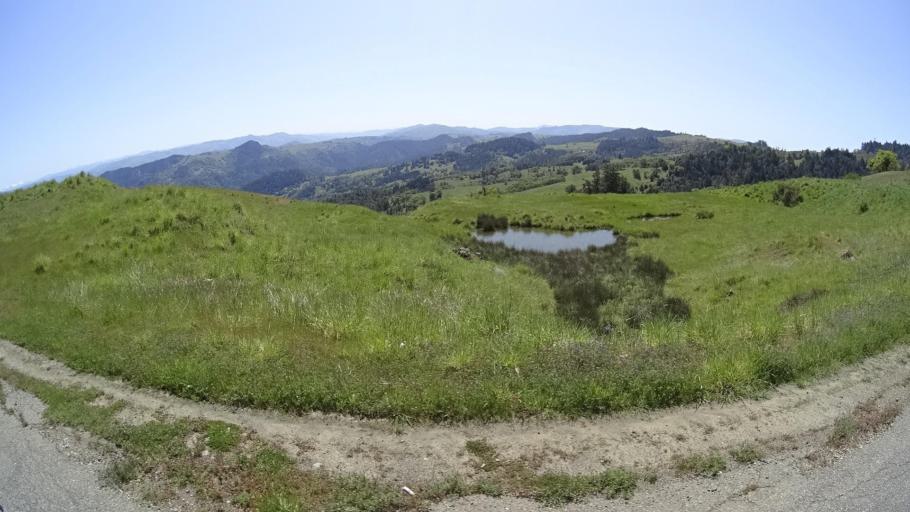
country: US
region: California
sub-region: Humboldt County
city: Redway
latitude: 40.1076
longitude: -123.6715
